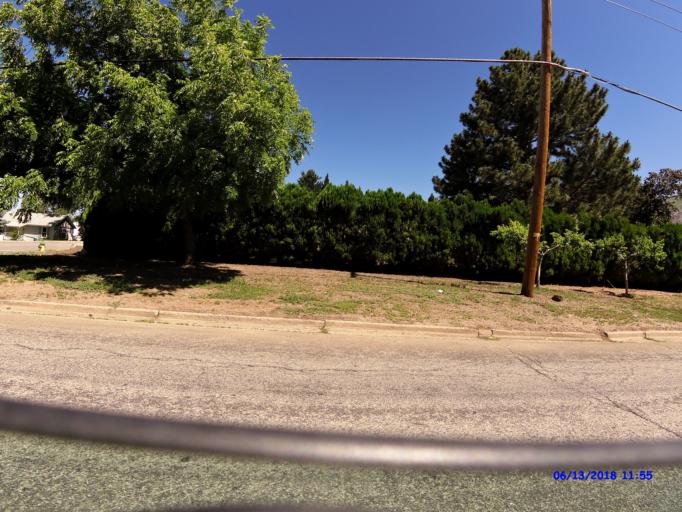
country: US
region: Utah
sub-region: Weber County
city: Ogden
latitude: 41.2287
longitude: -111.9451
